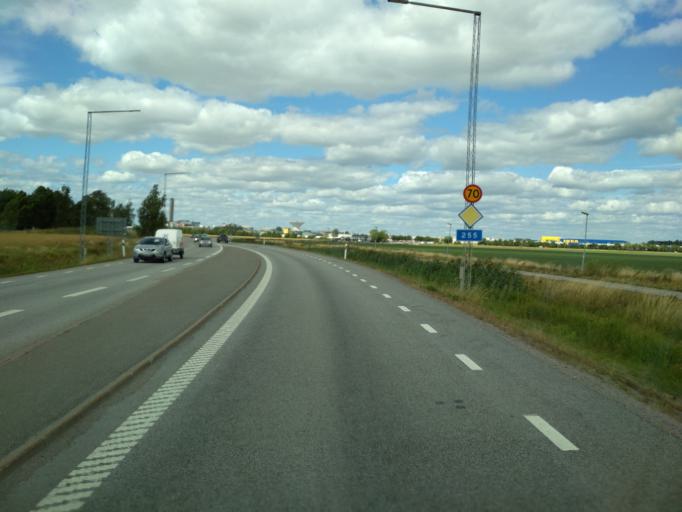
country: SE
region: Uppsala
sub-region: Uppsala Kommun
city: Saevja
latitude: 59.8368
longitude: 17.6914
